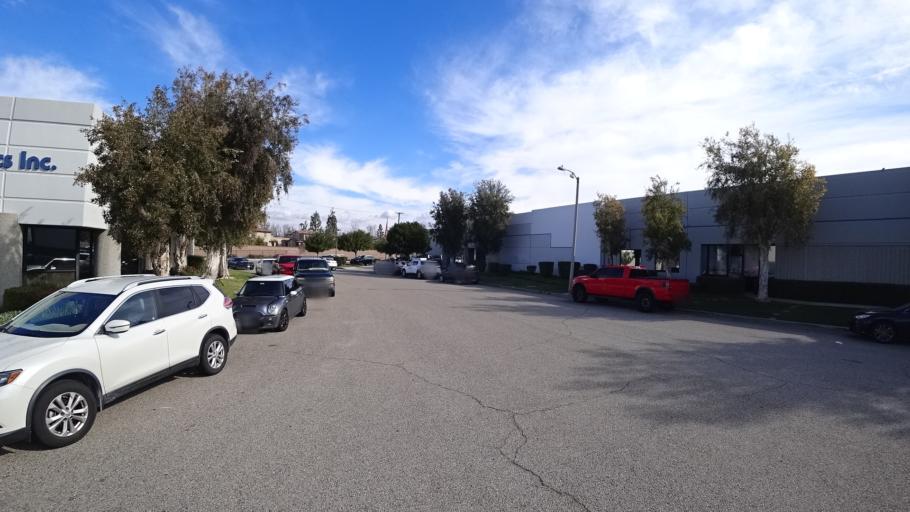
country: US
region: California
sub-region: Orange County
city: Placentia
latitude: 33.8678
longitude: -117.8701
